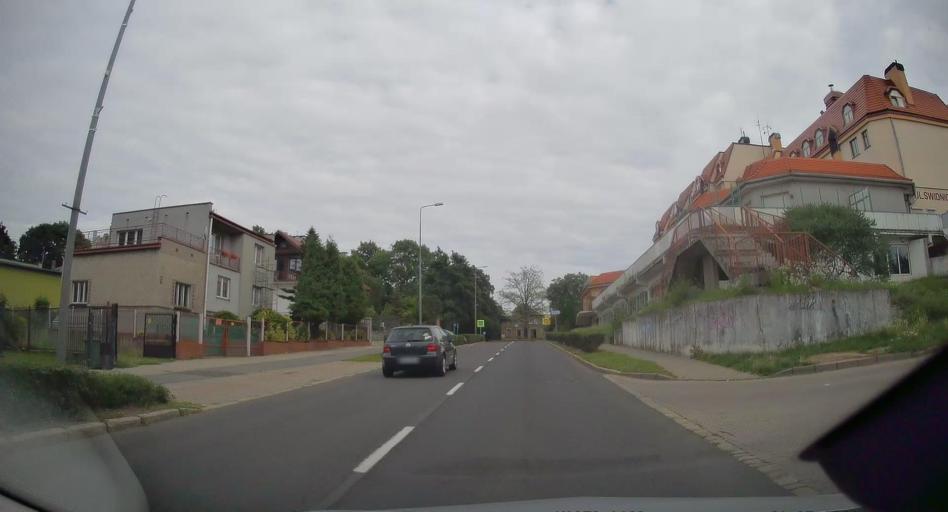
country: PL
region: Lower Silesian Voivodeship
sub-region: Powiat swidnicki
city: Swiebodzice
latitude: 50.8568
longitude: 16.3266
